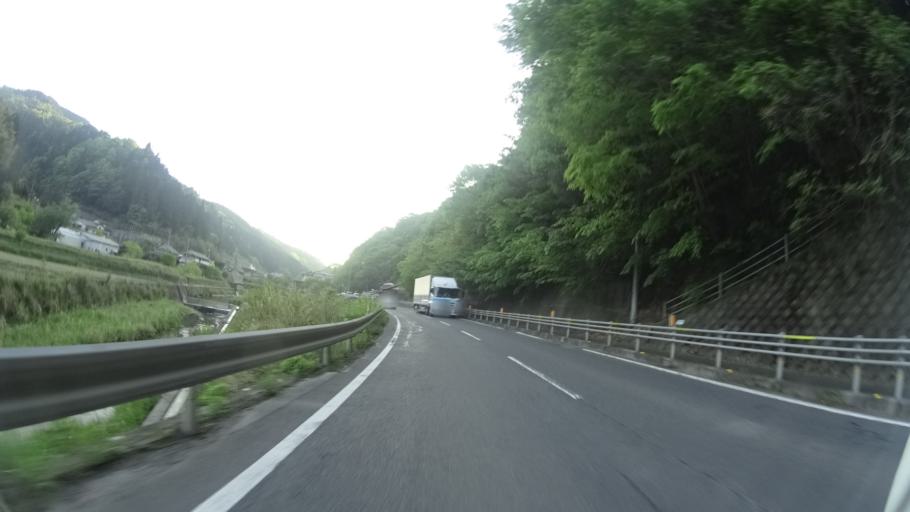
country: JP
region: Tokushima
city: Ikedacho
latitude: 34.0100
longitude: 133.7295
